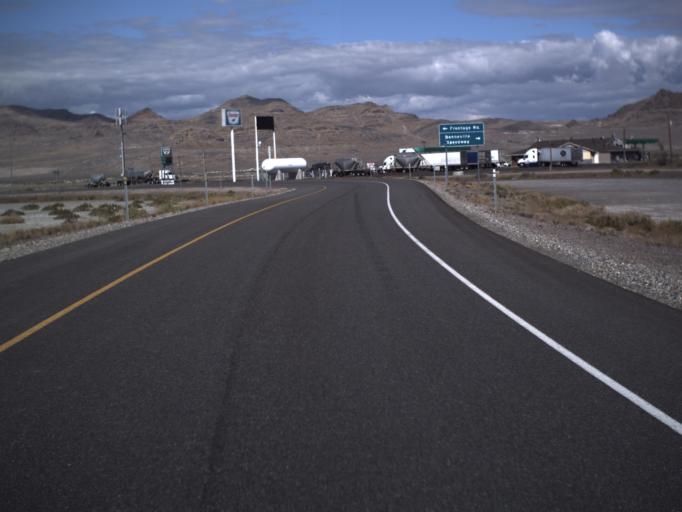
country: US
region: Utah
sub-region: Tooele County
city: Wendover
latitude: 40.7430
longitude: -113.9678
